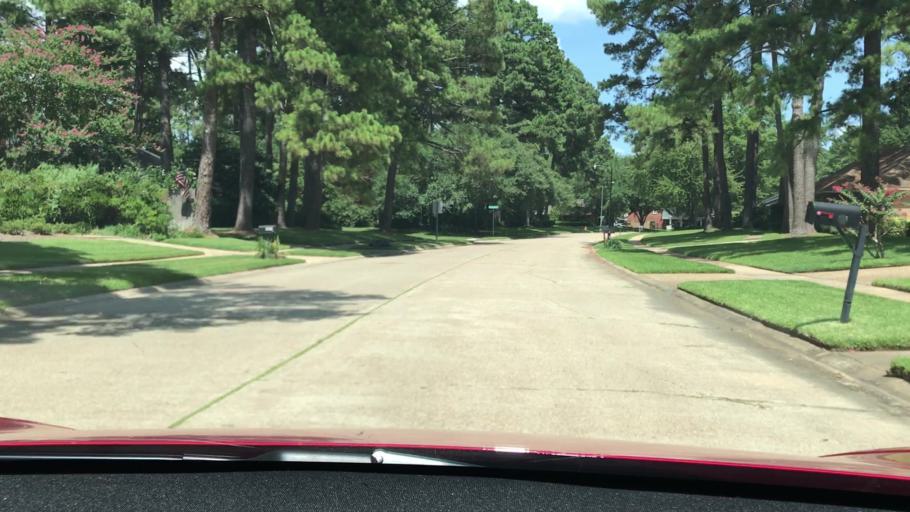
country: US
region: Louisiana
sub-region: Bossier Parish
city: Bossier City
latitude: 32.4229
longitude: -93.7341
